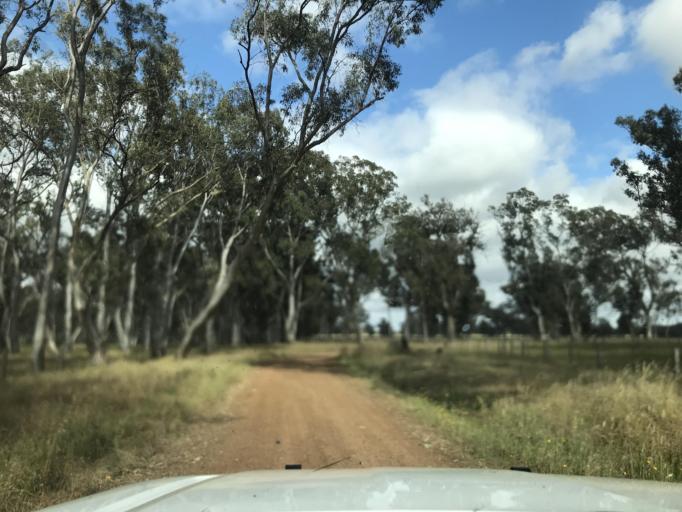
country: AU
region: South Australia
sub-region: Wattle Range
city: Penola
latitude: -37.1950
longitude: 141.0017
